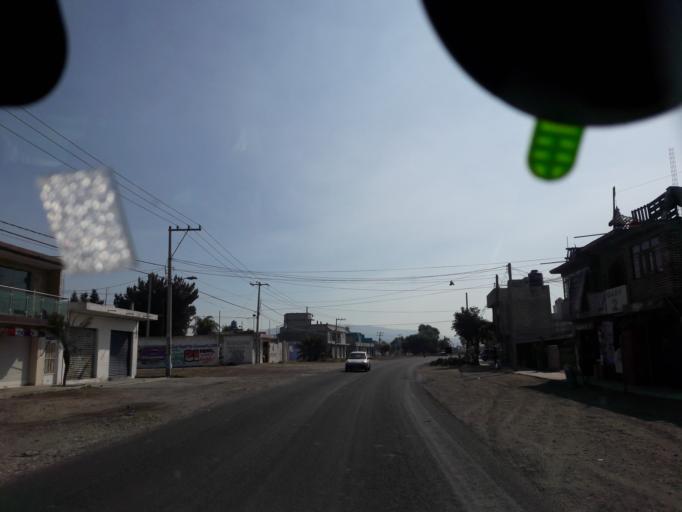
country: MX
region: Tlaxcala
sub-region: Ixtacuixtla de Mariano Matamoros
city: Santa Justina Ecatepec
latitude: 19.3102
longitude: -98.3506
